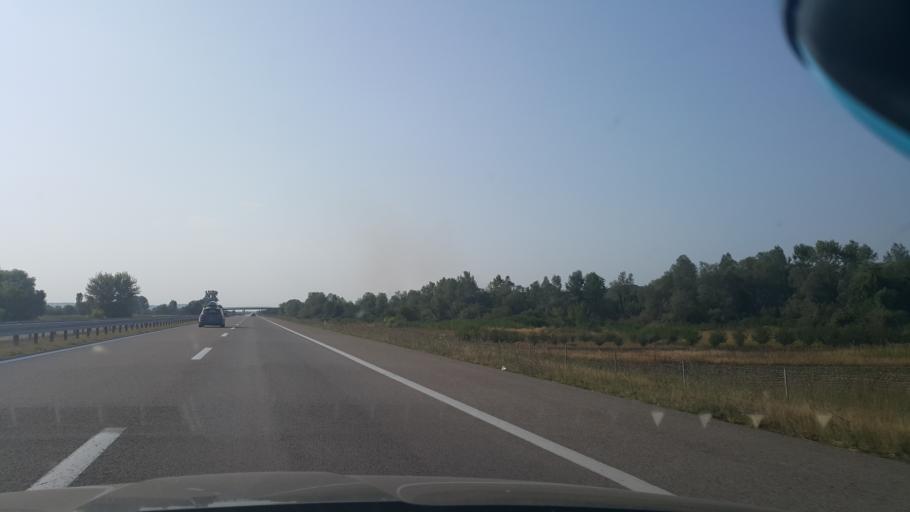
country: RS
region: Central Serbia
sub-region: Jablanicki Okrug
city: Leskovac
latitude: 43.0371
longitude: 21.9971
